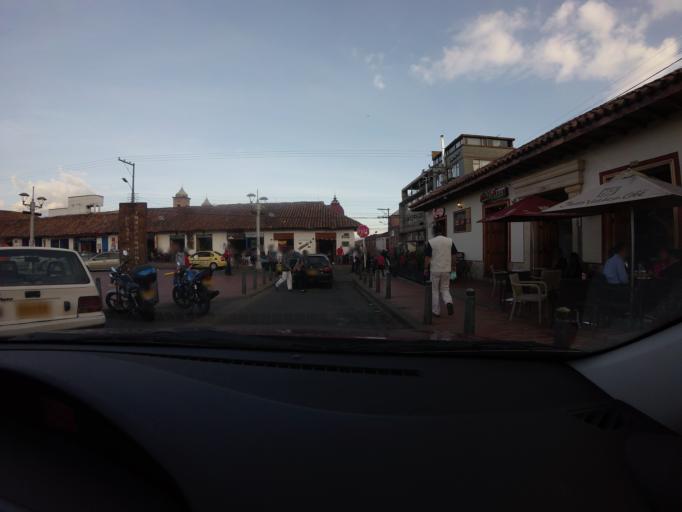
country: CO
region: Cundinamarca
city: Zipaquira
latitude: 5.0240
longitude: -74.0053
